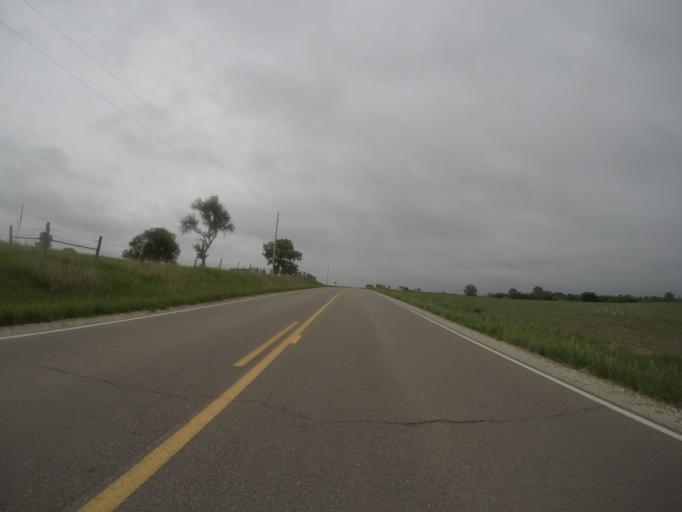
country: US
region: Kansas
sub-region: Pottawatomie County
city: Westmoreland
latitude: 39.5116
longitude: -96.2142
